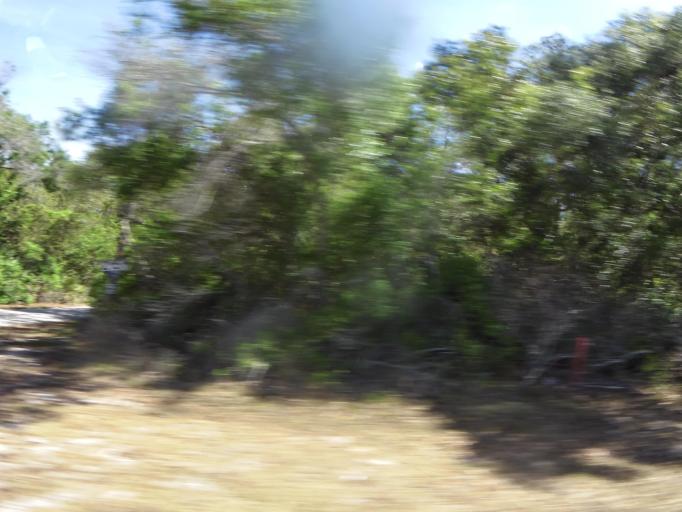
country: US
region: Florida
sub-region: Volusia County
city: Lake Helen
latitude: 28.9318
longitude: -81.2003
